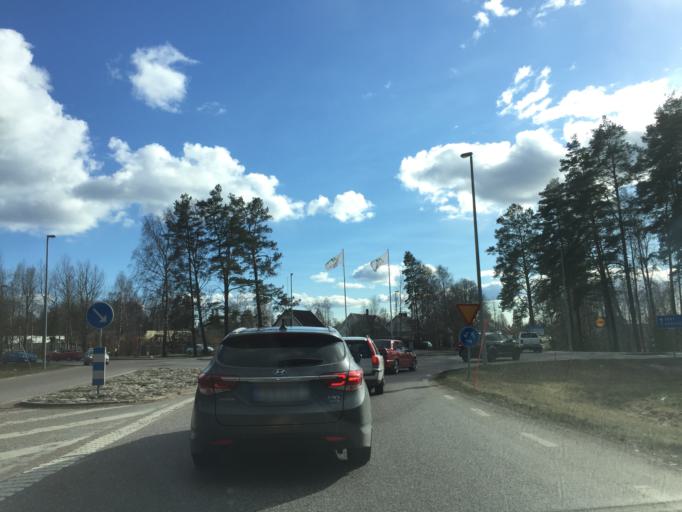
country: SE
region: OErebro
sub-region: Kumla Kommun
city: Kumla
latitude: 59.1432
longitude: 15.1381
